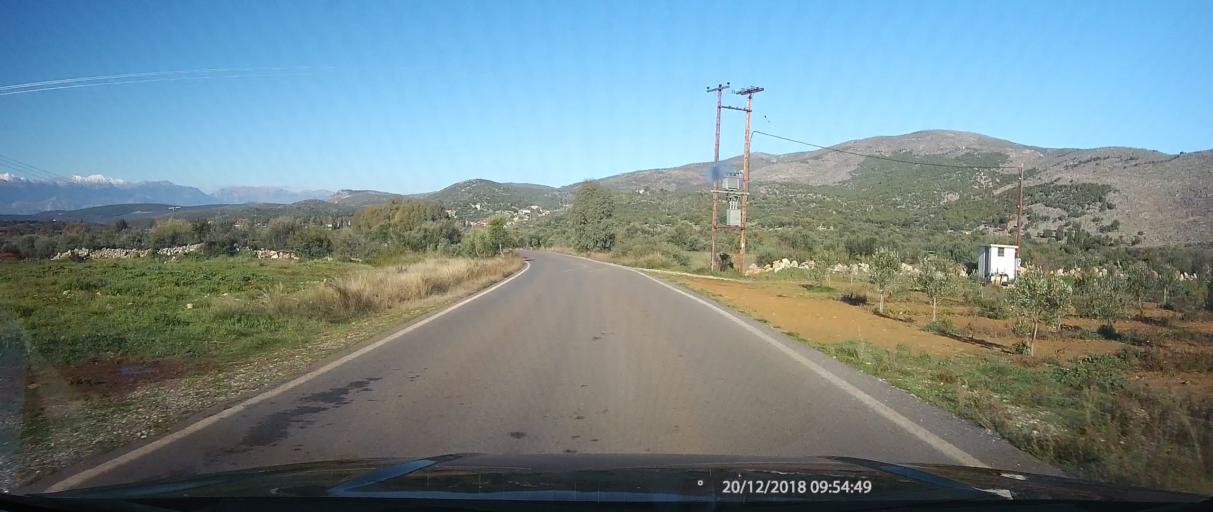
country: GR
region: Peloponnese
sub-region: Nomos Lakonias
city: Yerakion
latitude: 37.0202
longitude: 22.6308
